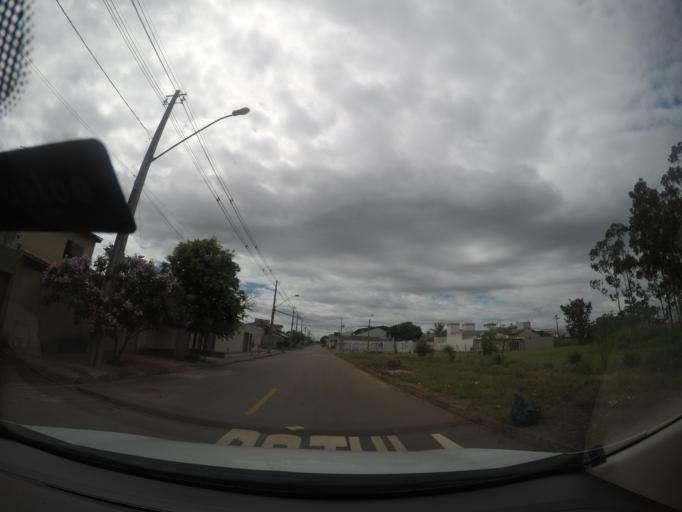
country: BR
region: Goias
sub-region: Goiania
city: Goiania
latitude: -16.7271
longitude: -49.3449
